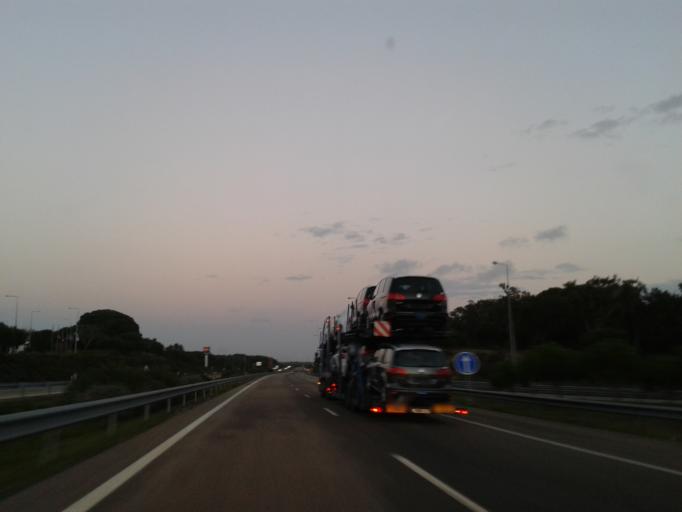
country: PT
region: Evora
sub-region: Vendas Novas
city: Vendas Novas
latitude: 38.6214
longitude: -8.5797
